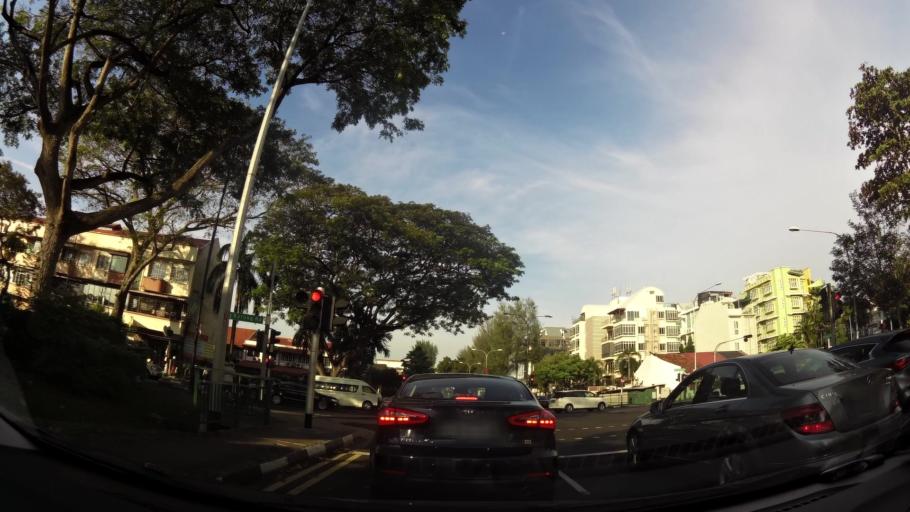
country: SG
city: Singapore
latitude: 1.3094
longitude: 103.8946
